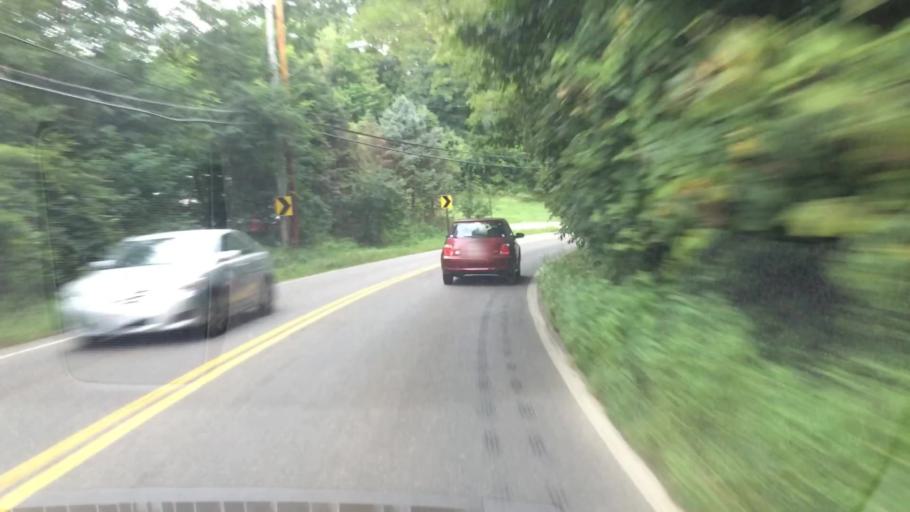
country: US
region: Ohio
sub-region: Summit County
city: Cuyahoga Falls
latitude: 41.1308
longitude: -81.5272
